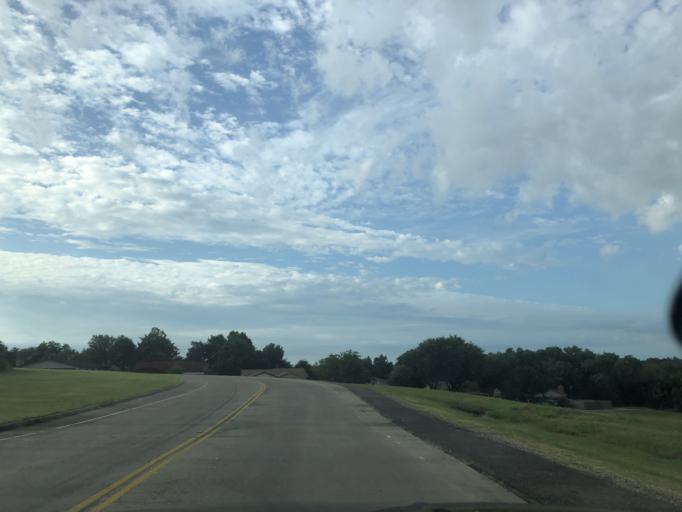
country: US
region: Texas
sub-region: Dallas County
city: Sunnyvale
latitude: 32.8445
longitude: -96.5829
